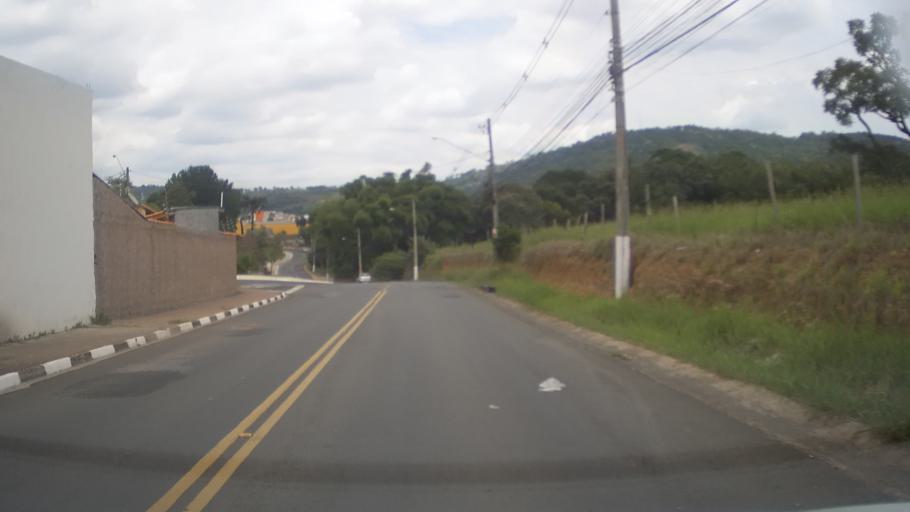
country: BR
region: Sao Paulo
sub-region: Itupeva
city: Itupeva
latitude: -23.1530
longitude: -47.0452
